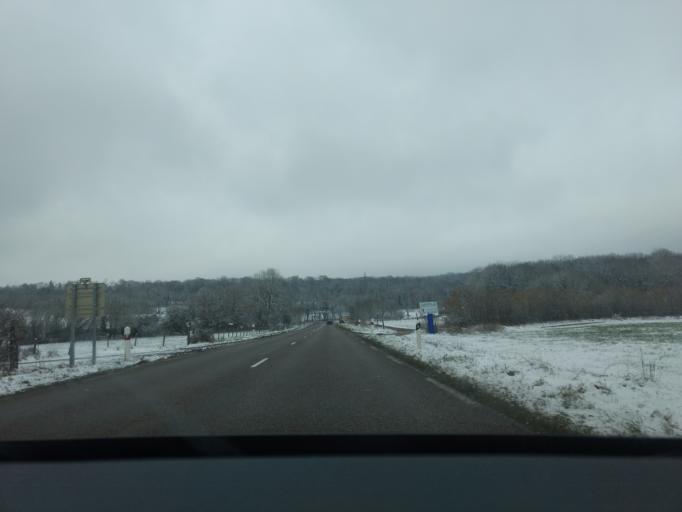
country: FR
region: Franche-Comte
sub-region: Departement du Jura
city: Champagnole
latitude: 46.8047
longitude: 5.8262
